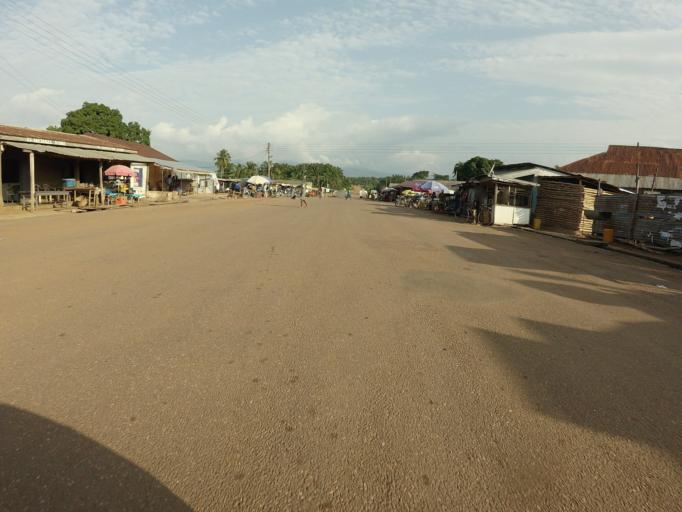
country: GH
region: Volta
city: Kpandu
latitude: 6.9978
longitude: 0.4385
